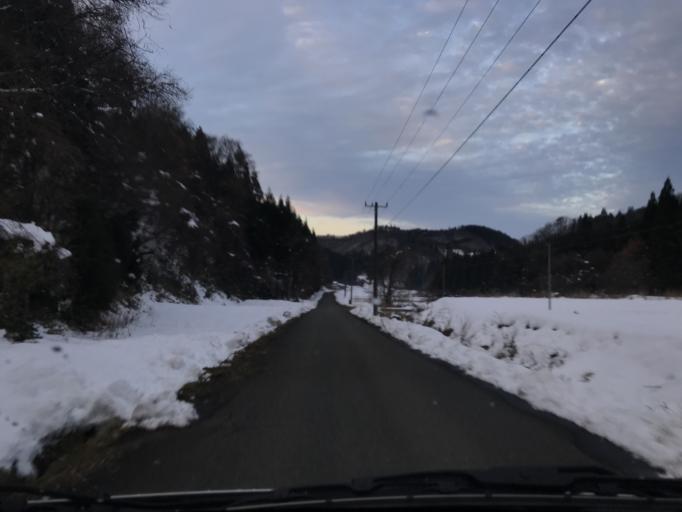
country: JP
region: Iwate
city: Mizusawa
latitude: 39.0413
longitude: 141.0106
